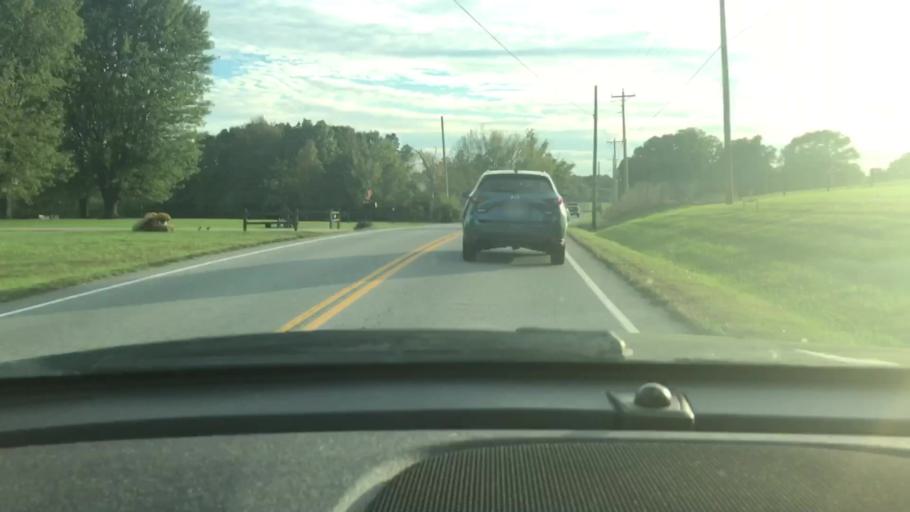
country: US
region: Tennessee
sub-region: Dickson County
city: Charlotte
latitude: 36.2345
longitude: -87.2481
